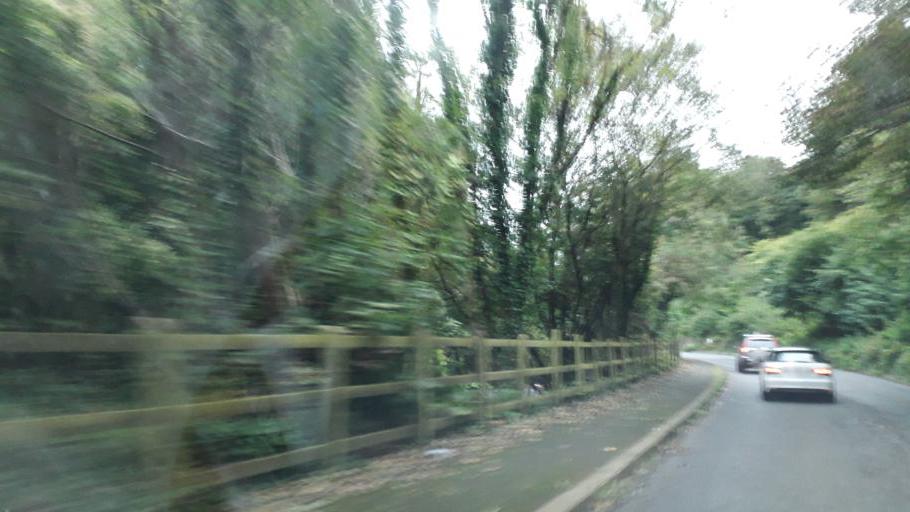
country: IE
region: Leinster
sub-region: Wicklow
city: Enniskerry
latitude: 53.1908
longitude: -6.1571
